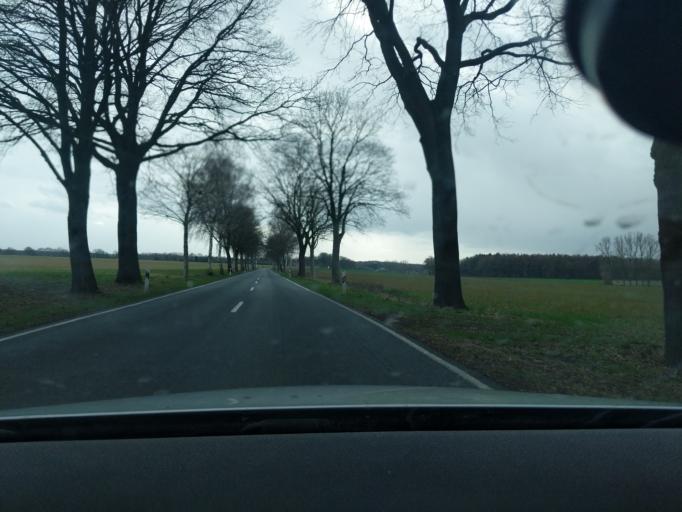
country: DE
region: Lower Saxony
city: Bliedersdorf
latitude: 53.4957
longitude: 9.5323
